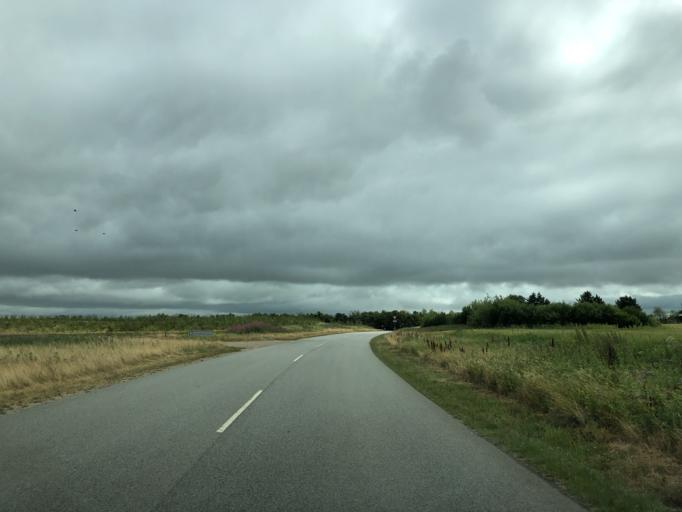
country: DK
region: Central Jutland
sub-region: Herning Kommune
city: Vildbjerg
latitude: 56.1849
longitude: 8.7547
